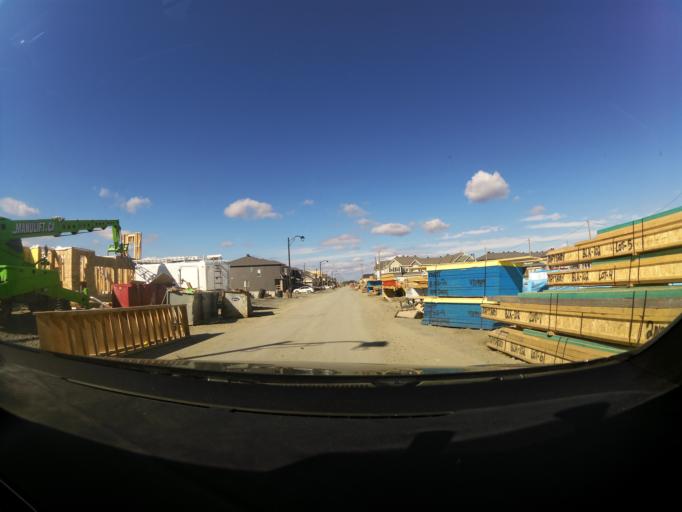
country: CA
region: Ontario
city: Bells Corners
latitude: 45.2804
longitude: -75.8899
